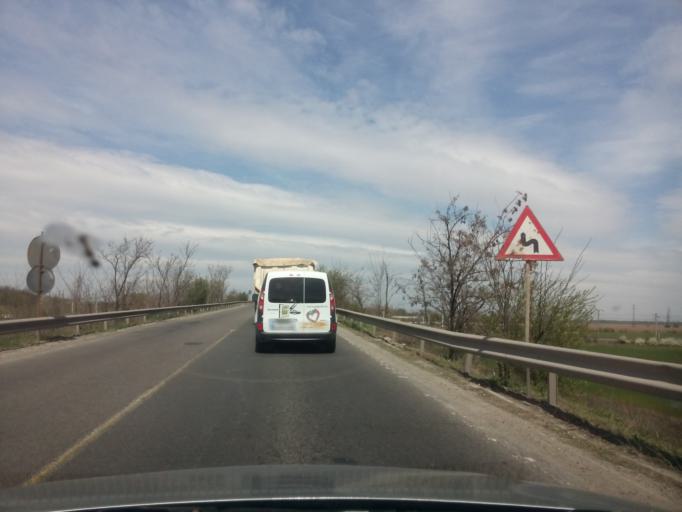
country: RO
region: Ilfov
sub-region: Comuna Pantelimon
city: Pantelimon
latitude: 44.4716
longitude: 26.2315
